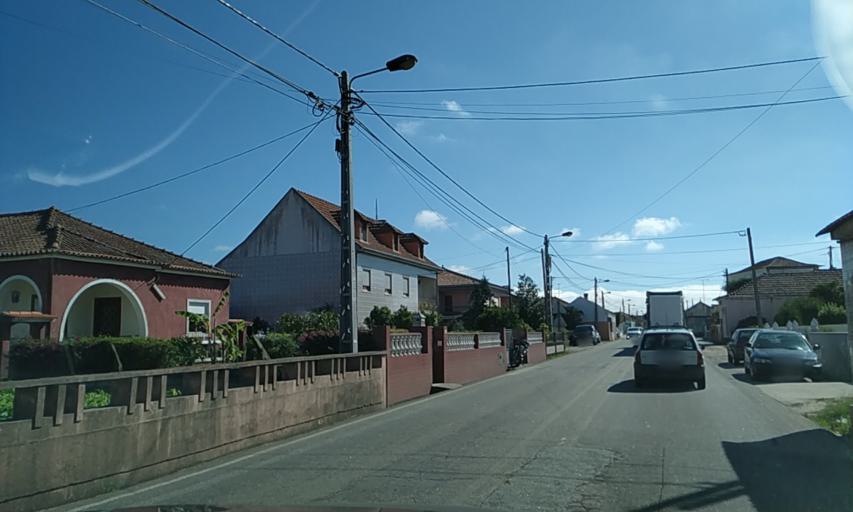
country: PT
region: Aveiro
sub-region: Aveiro
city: Aveiro
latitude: 40.6779
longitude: -8.5983
